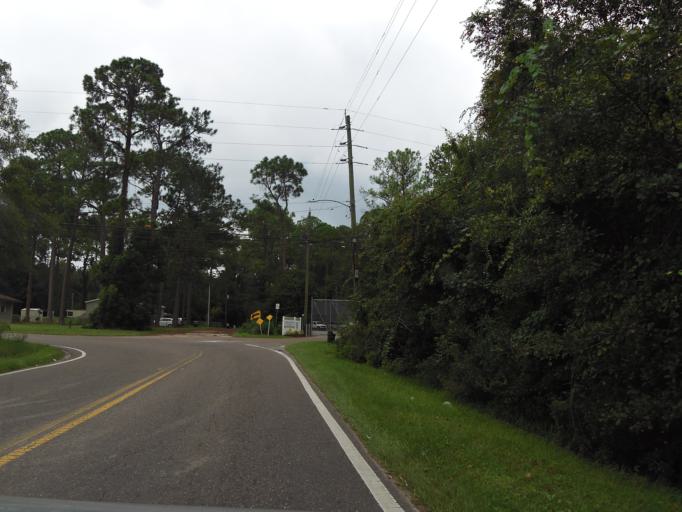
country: US
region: Florida
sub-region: Clay County
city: Bellair-Meadowbrook Terrace
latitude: 30.2116
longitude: -81.7728
